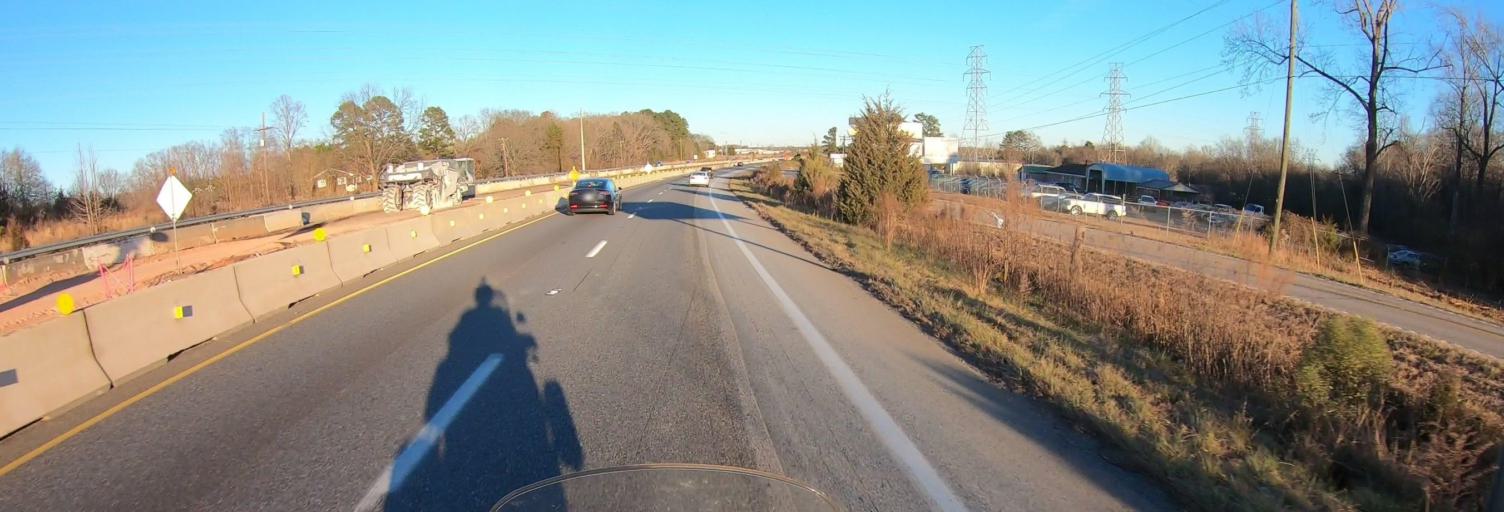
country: US
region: South Carolina
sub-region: Cherokee County
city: East Gaffney
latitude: 35.1003
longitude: -81.6415
